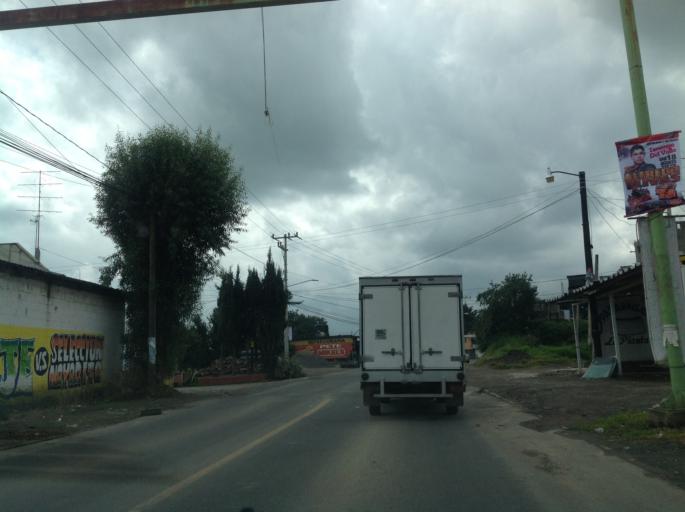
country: MX
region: Mexico
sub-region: Tenango del Valle
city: Santa Maria Jajalpa
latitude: 19.1162
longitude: -99.5412
